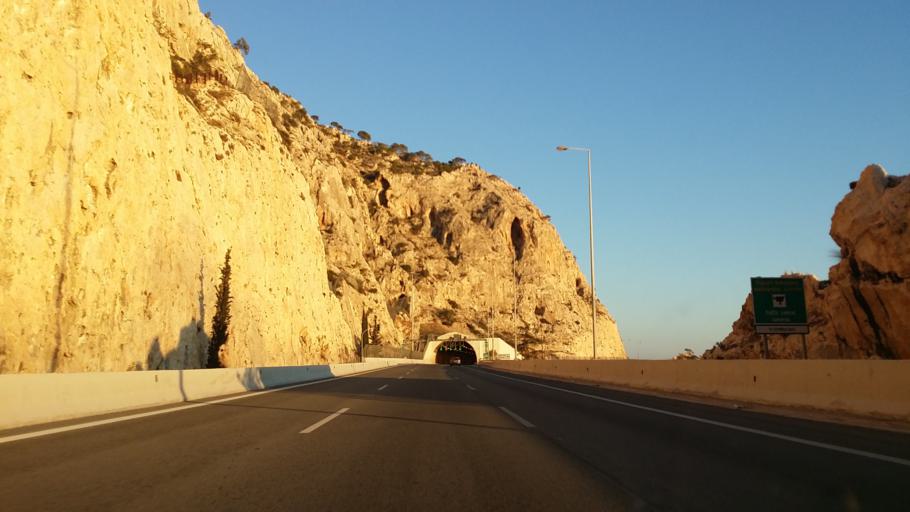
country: GR
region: Attica
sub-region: Nomarchia Dytikis Attikis
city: Kineta
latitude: 37.9788
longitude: 23.2774
